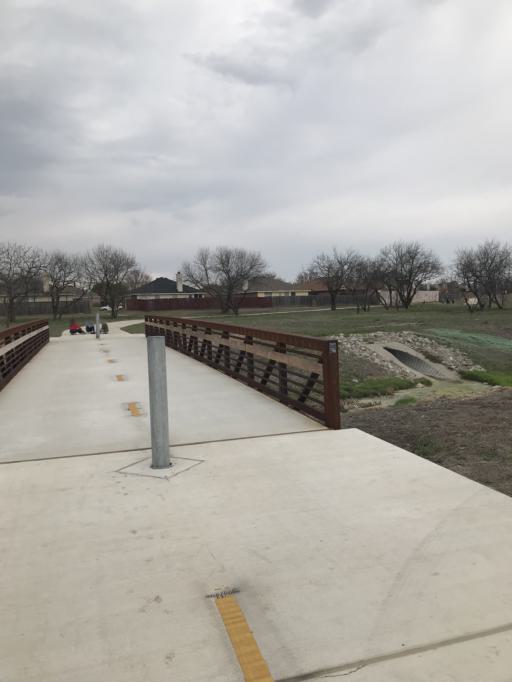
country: US
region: Texas
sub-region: Denton County
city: Denton
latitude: 33.2512
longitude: -97.1410
